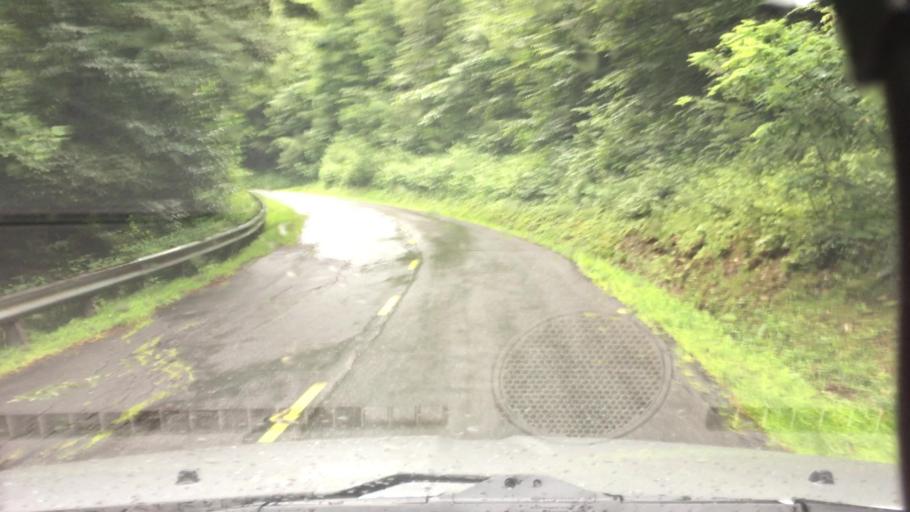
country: US
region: North Carolina
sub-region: Madison County
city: Mars Hill
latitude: 35.9426
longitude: -82.5173
